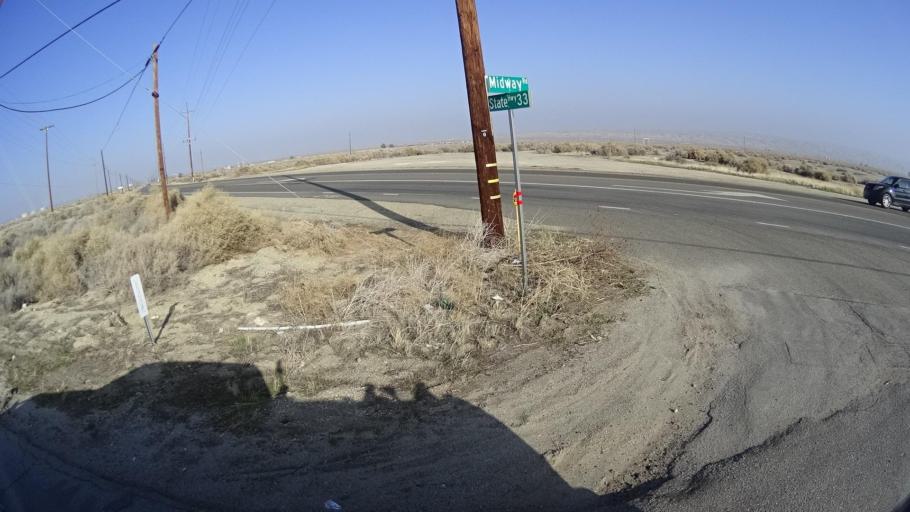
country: US
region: California
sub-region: Kern County
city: Taft Heights
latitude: 35.1801
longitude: -119.5277
